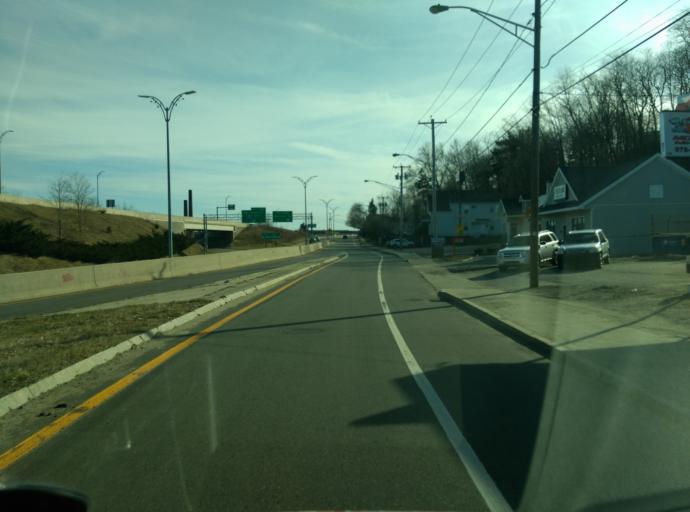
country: US
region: Massachusetts
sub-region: Essex County
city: North Andover
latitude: 42.7114
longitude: -71.1398
